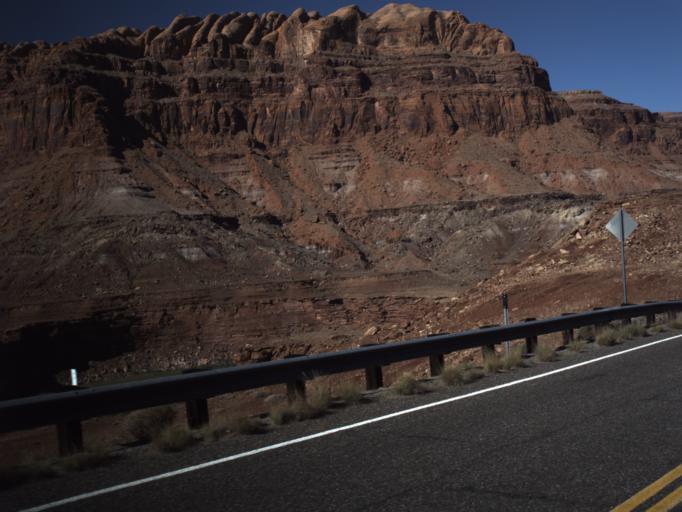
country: US
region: Utah
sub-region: San Juan County
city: Blanding
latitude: 37.8827
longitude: -110.4240
